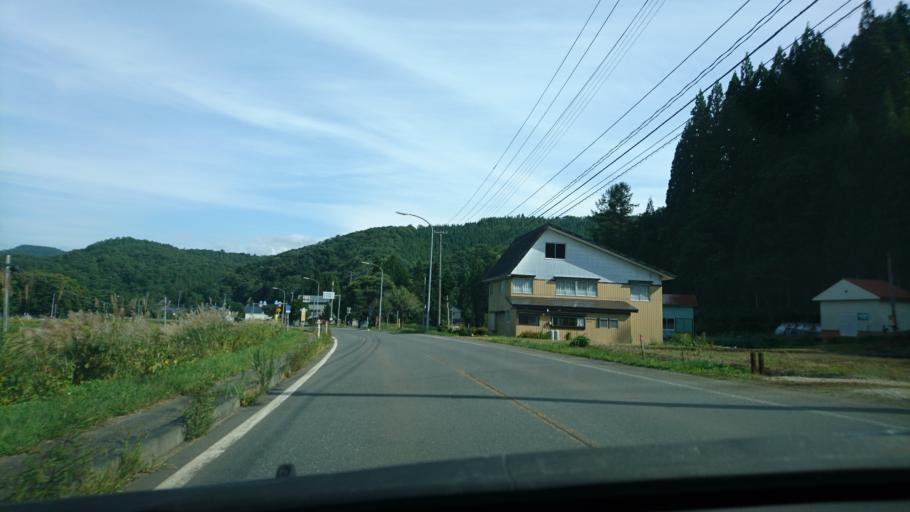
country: JP
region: Akita
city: Yokotemachi
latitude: 39.3113
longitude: 140.7599
